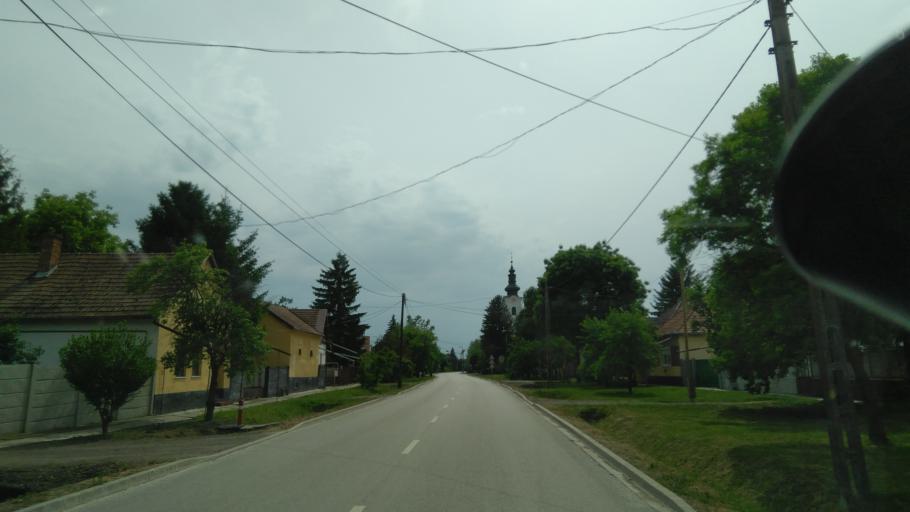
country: HU
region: Bekes
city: Mehkerek
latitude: 46.8706
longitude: 21.5242
